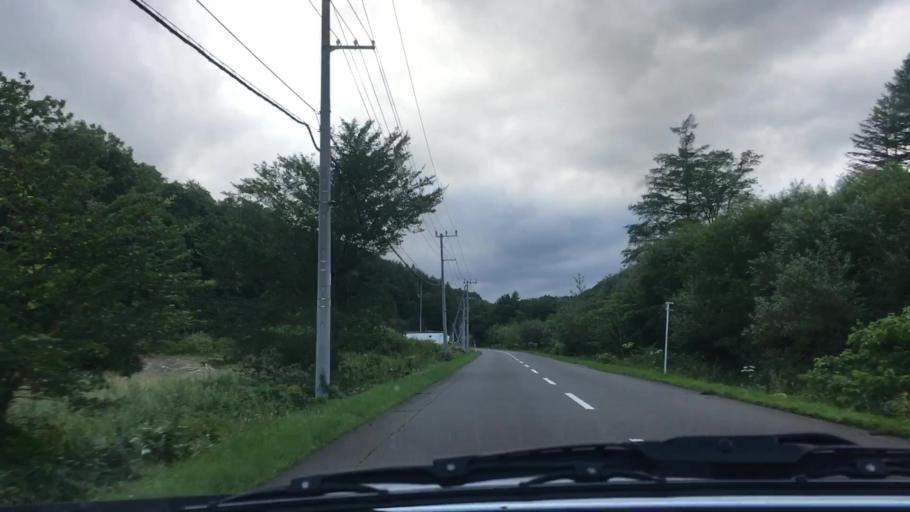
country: JP
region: Hokkaido
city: Otofuke
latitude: 43.1424
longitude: 142.8828
